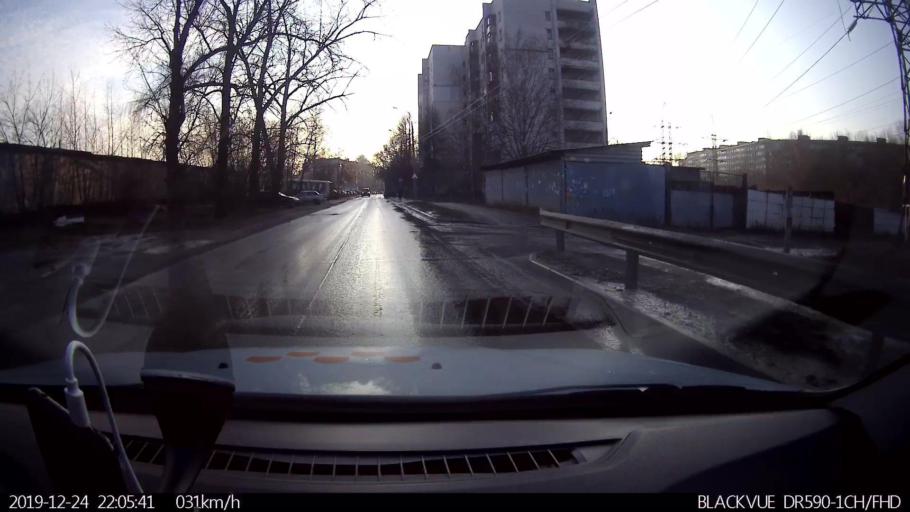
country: RU
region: Nizjnij Novgorod
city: Nizhniy Novgorod
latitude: 56.3195
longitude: 43.8814
